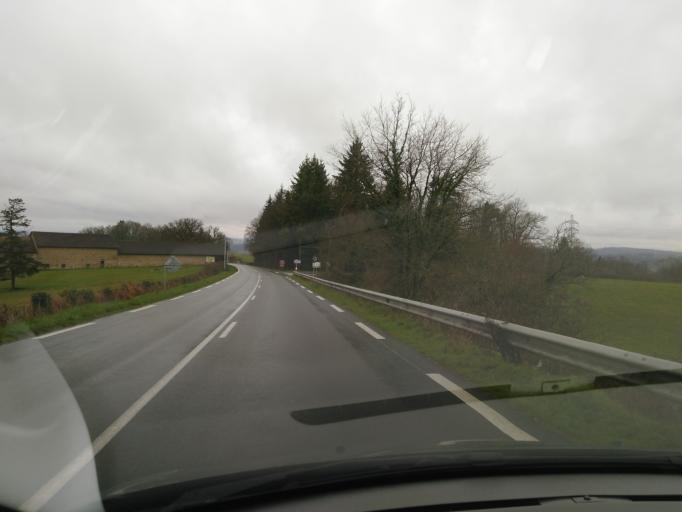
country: FR
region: Limousin
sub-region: Departement de la Haute-Vienne
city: Condat-sur-Vienne
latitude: 45.7715
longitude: 1.2895
